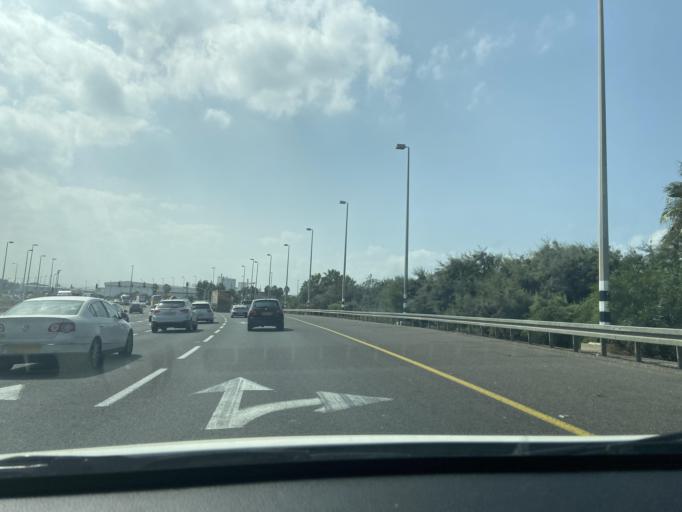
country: IL
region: Northern District
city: `Akko
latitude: 32.9064
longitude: 35.0906
